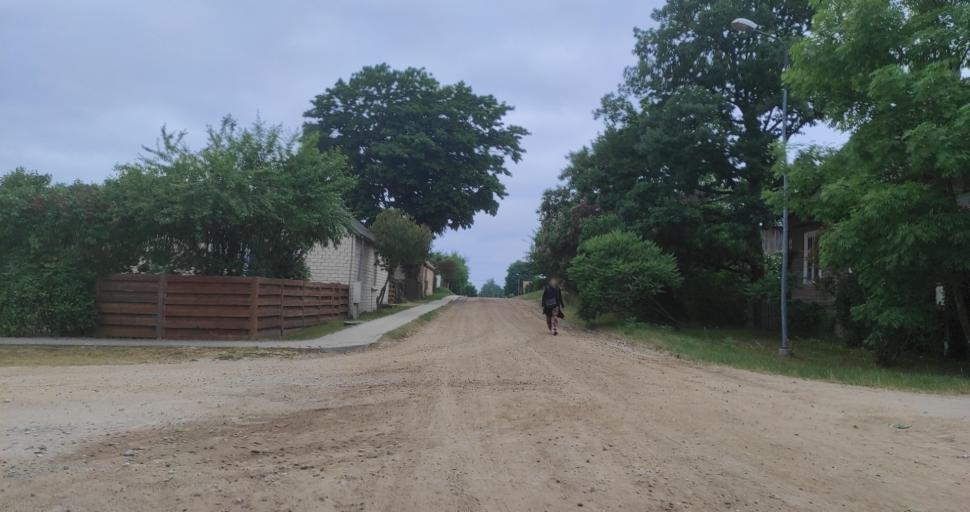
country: LV
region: Pavilostas
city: Pavilosta
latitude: 56.8892
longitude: 21.1863
